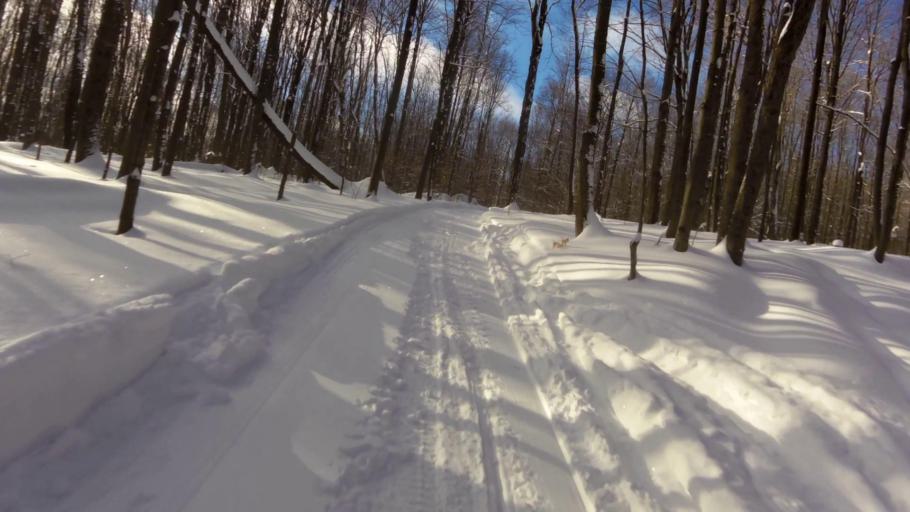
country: US
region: New York
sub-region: Chautauqua County
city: Falconer
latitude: 42.2492
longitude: -79.1521
